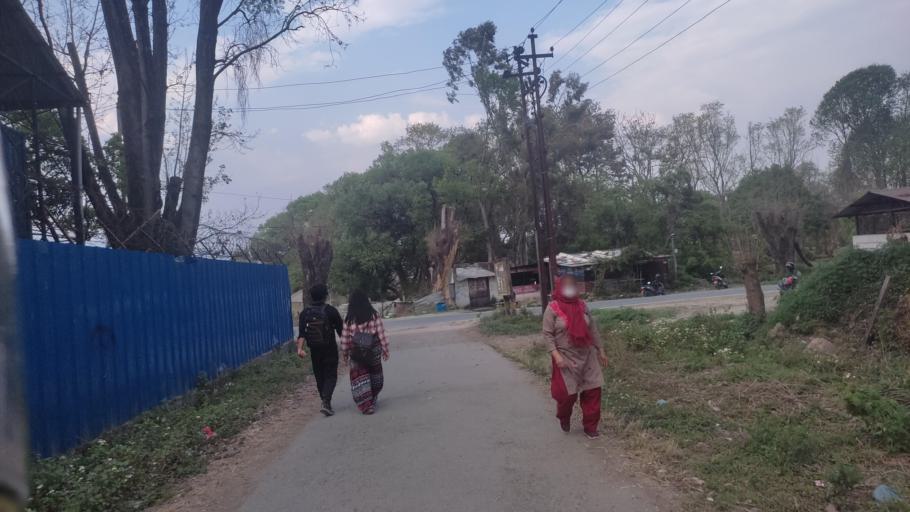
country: NP
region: Central Region
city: Kirtipur
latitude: 27.6822
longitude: 85.2859
